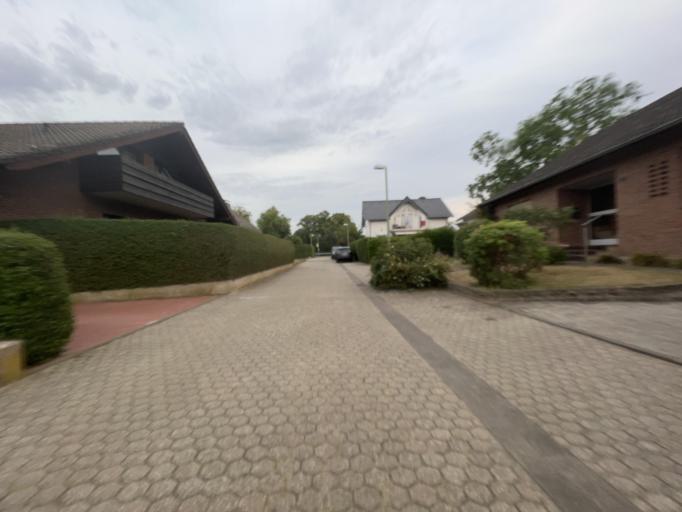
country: DE
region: North Rhine-Westphalia
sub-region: Regierungsbezirk Koln
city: Kreuzau
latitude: 50.7756
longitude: 6.4500
